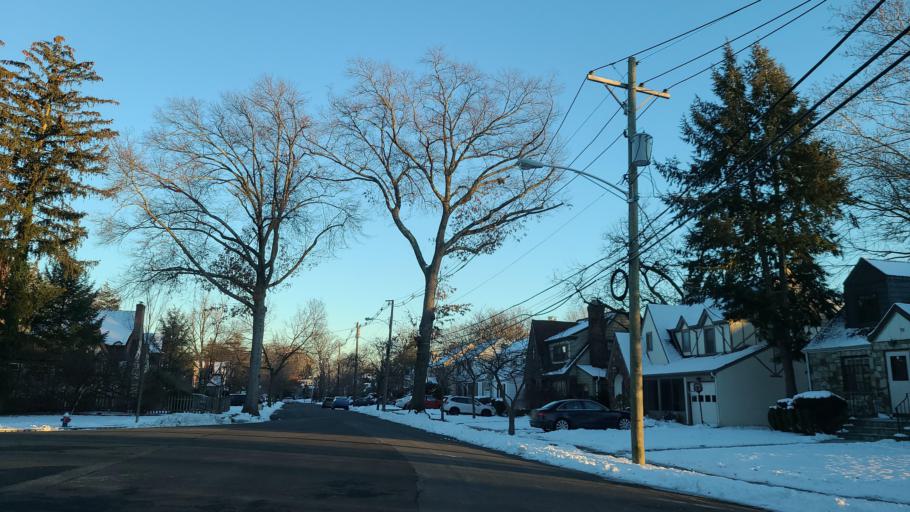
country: US
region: New Jersey
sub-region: Union County
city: Springfield
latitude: 40.7184
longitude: -74.3037
